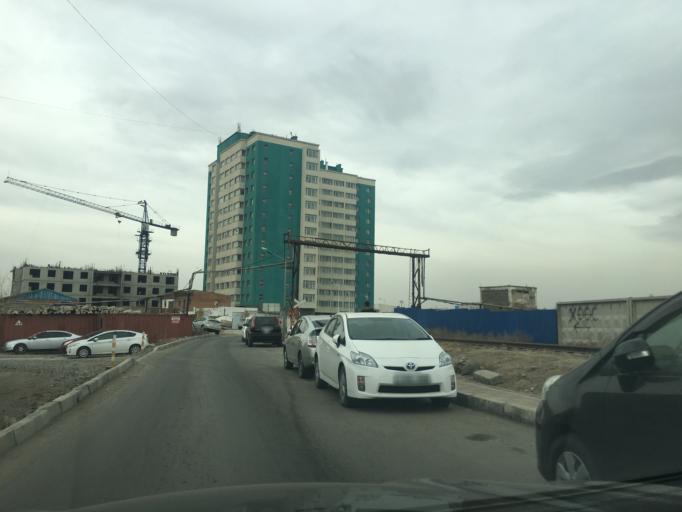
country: MN
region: Ulaanbaatar
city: Ulaanbaatar
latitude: 47.9046
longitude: 106.8885
